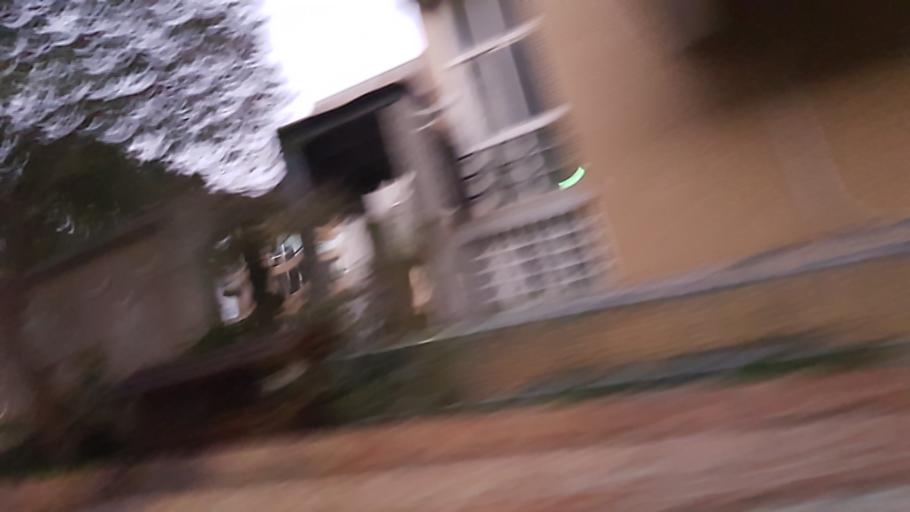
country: TW
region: Taiwan
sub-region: Hsinchu
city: Hsinchu
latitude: 24.7900
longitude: 120.9682
